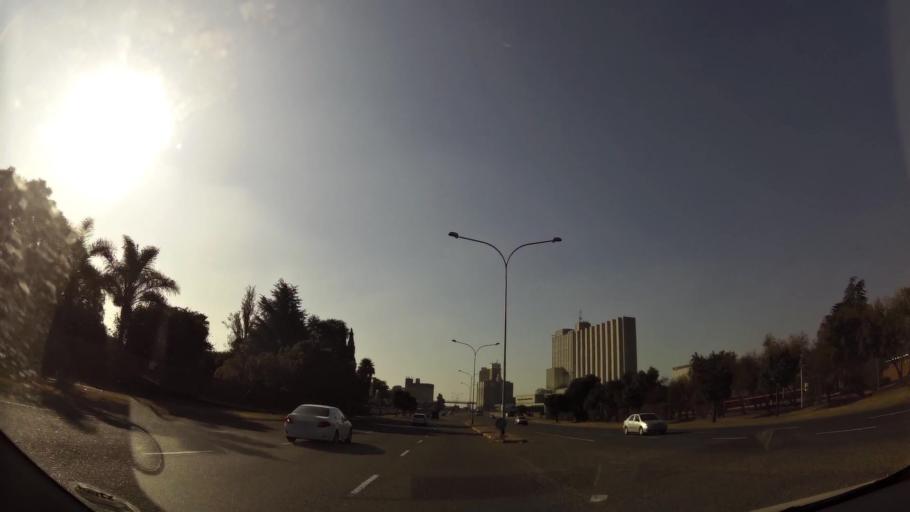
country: ZA
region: Gauteng
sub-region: West Rand District Municipality
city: Randfontein
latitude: -26.1687
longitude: 27.7118
